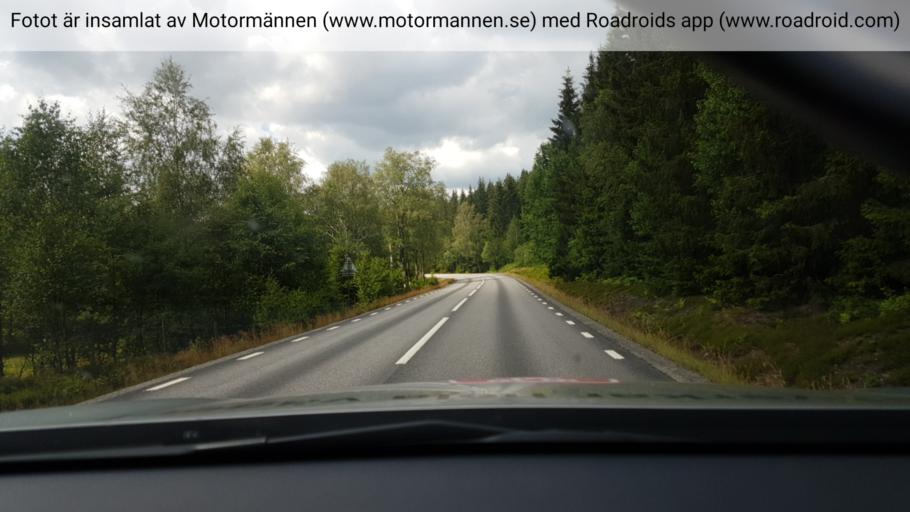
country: SE
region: Vaestra Goetaland
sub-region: Tranemo Kommun
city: Tranemo
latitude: 57.4750
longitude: 13.2770
